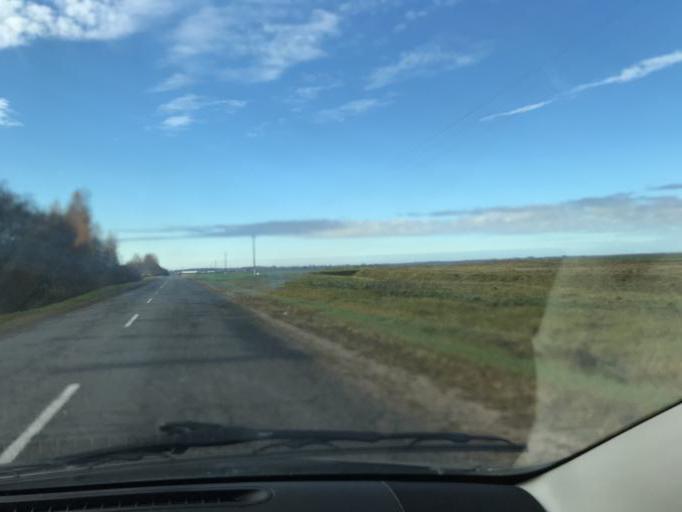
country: BY
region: Vitebsk
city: Haradok
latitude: 55.3877
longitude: 29.6640
